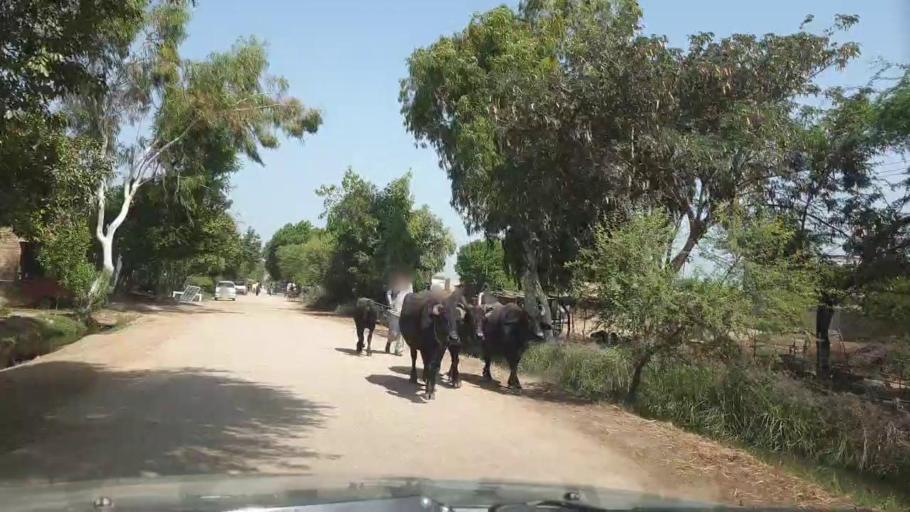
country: PK
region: Sindh
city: Tando Ghulam Ali
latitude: 25.1043
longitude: 68.7670
